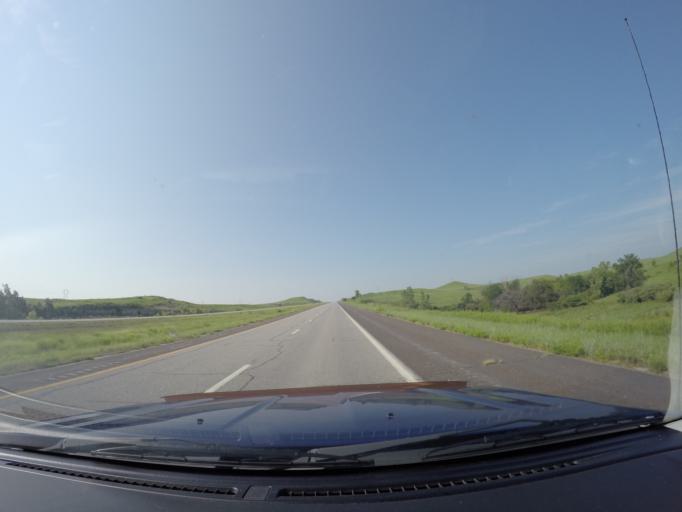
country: US
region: Kansas
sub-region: Riley County
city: Manhattan
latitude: 39.0830
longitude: -96.5386
